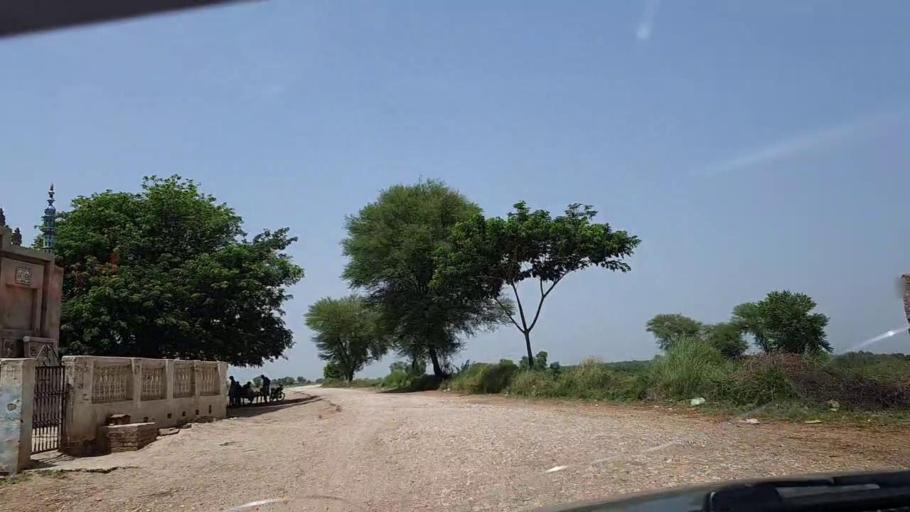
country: PK
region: Sindh
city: Tharu Shah
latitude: 26.9157
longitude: 68.0604
